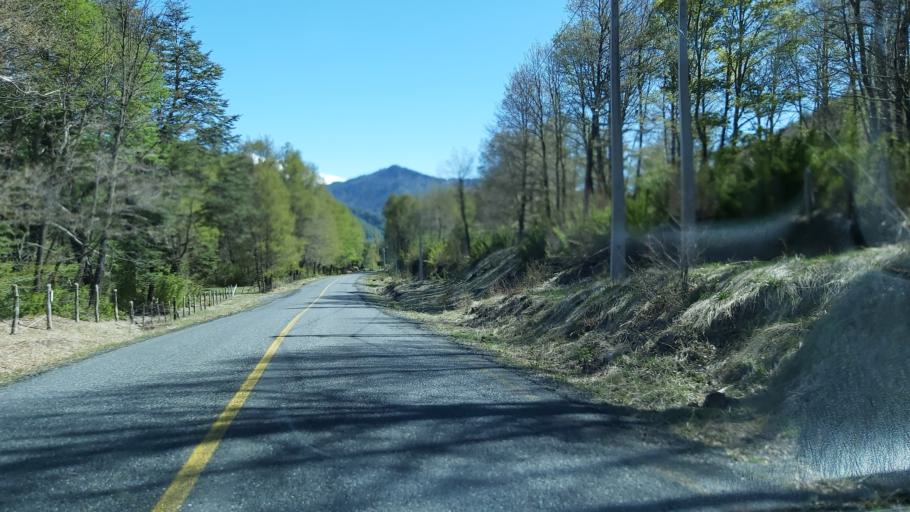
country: CL
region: Araucania
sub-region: Provincia de Cautin
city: Vilcun
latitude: -38.4653
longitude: -71.5190
